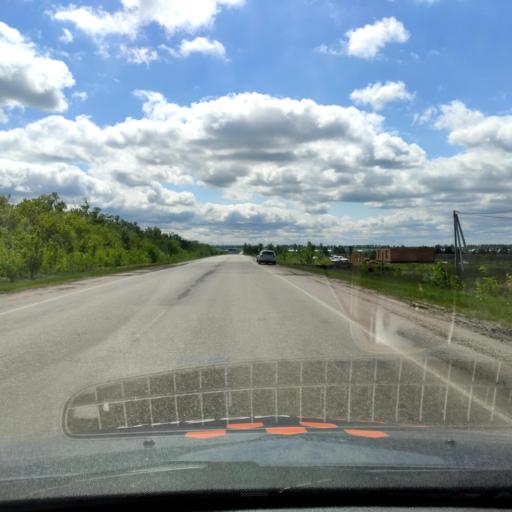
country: RU
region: Voronezj
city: Novaya Usman'
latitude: 51.6144
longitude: 39.3366
